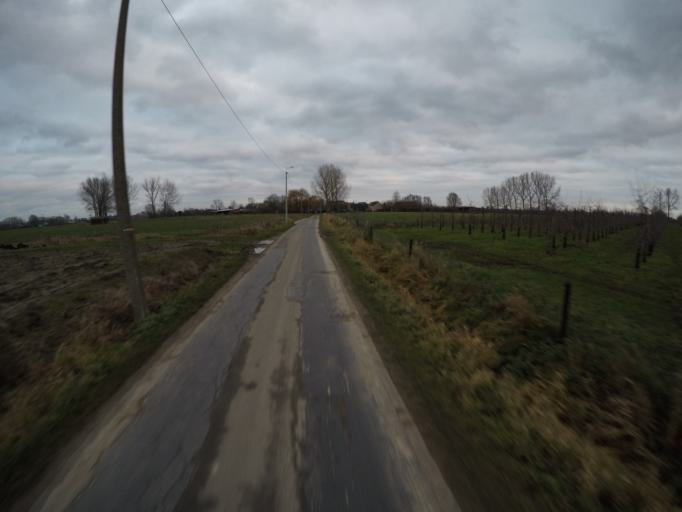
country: BE
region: Flanders
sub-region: Provincie Oost-Vlaanderen
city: Sint-Gillis-Waas
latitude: 51.2238
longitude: 4.1776
